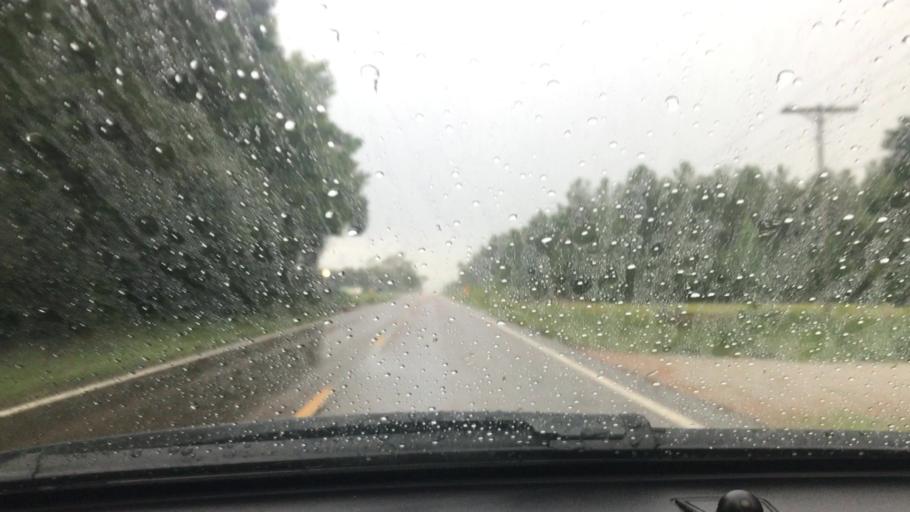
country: US
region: Mississippi
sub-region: Pike County
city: Summit
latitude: 31.3137
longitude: -90.5235
